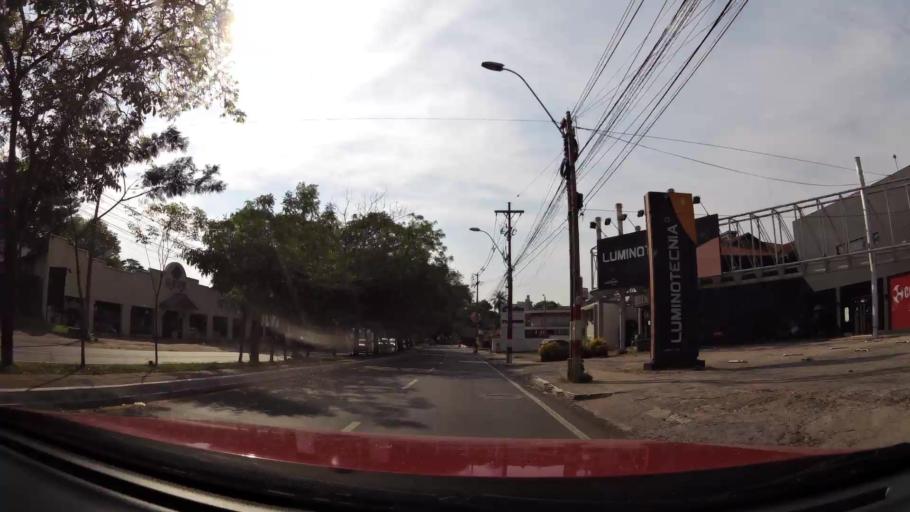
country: PY
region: Central
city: Lambare
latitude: -25.2980
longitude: -57.5710
